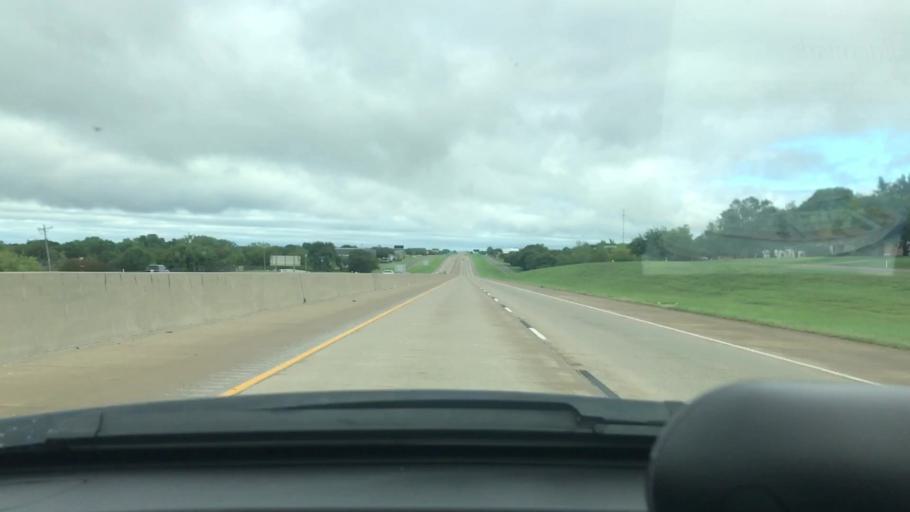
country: US
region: Texas
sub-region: Grayson County
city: Van Alstyne
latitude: 33.4402
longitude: -96.5989
